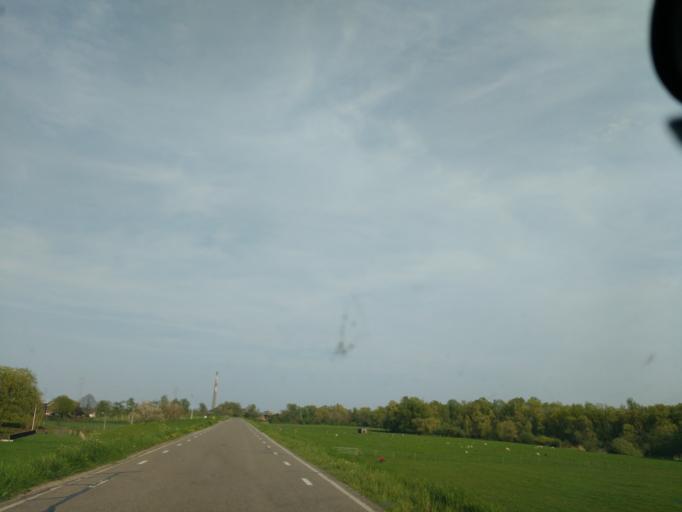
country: NL
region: Gelderland
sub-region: Gemeente Wageningen
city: Wageningen
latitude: 51.9483
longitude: 5.6211
